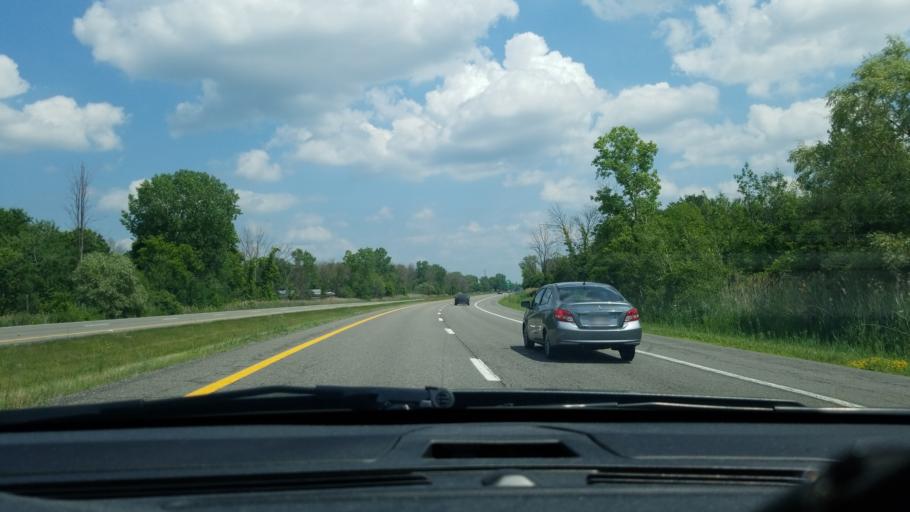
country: US
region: New York
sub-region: Onondaga County
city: North Syracuse
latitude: 43.1569
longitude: -76.1497
